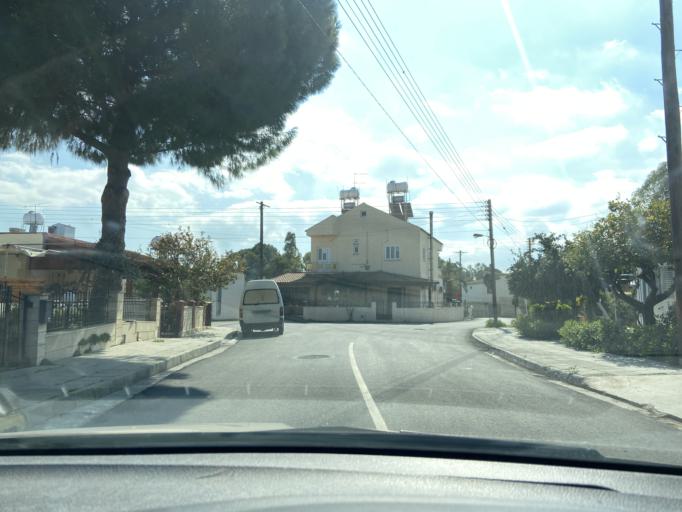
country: CY
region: Lefkosia
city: Dali
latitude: 35.0213
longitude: 33.3924
